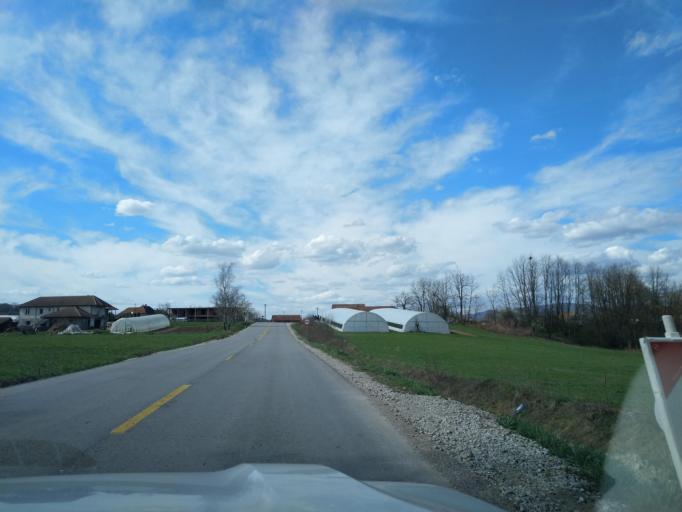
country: RS
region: Central Serbia
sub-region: Zlatiborski Okrug
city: Arilje
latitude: 43.7941
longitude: 20.1001
